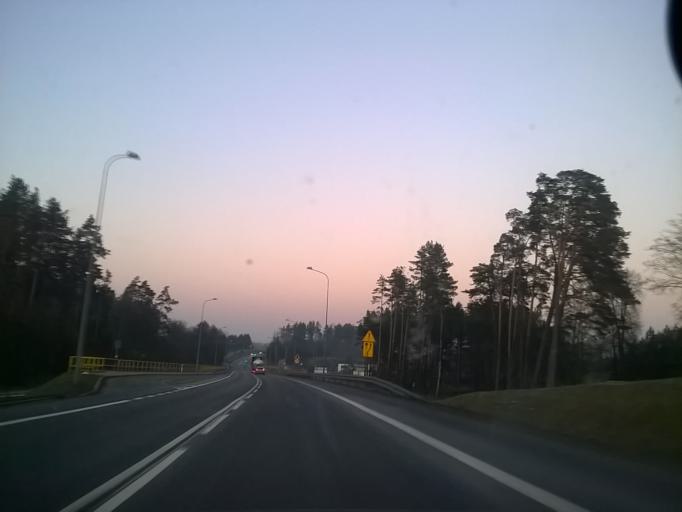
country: PL
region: Warmian-Masurian Voivodeship
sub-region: Powiat olsztynski
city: Barczewo
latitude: 53.8011
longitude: 20.6194
